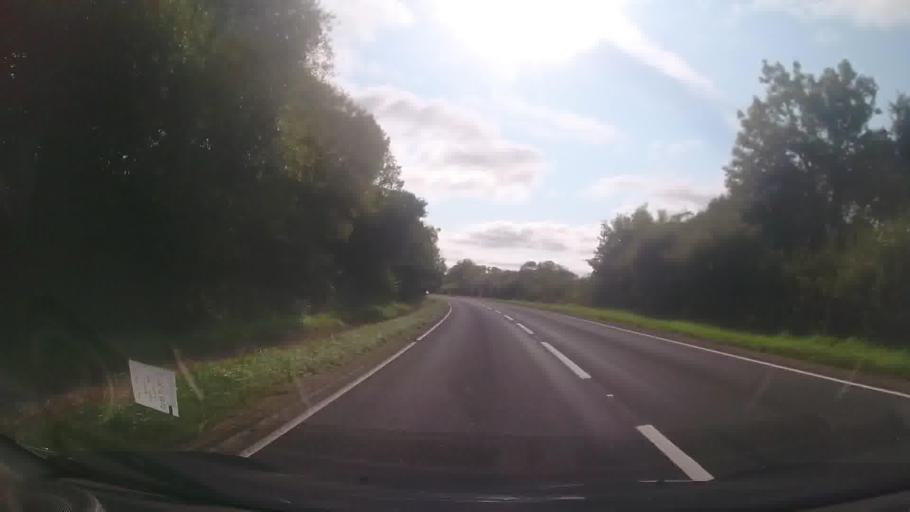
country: GB
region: Wales
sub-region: Pembrokeshire
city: Jeffreyston
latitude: 51.7133
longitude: -4.7617
